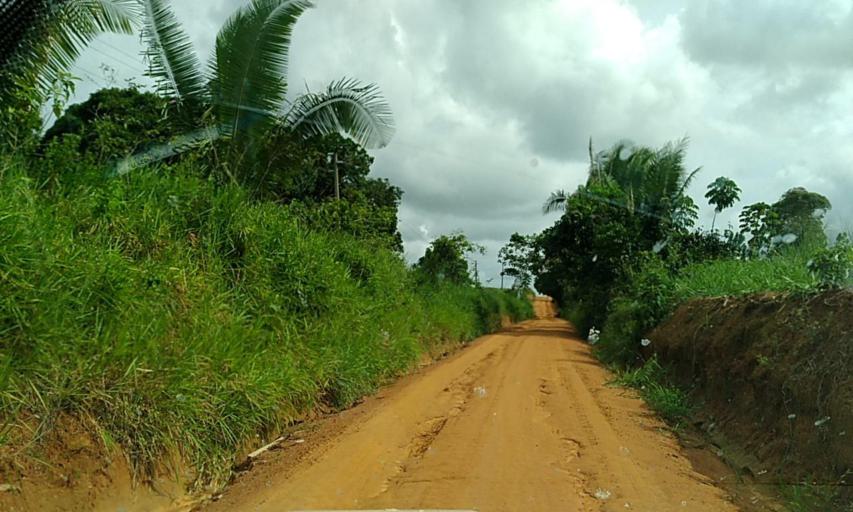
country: BR
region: Para
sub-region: Altamira
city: Altamira
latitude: -3.2965
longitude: -52.6880
